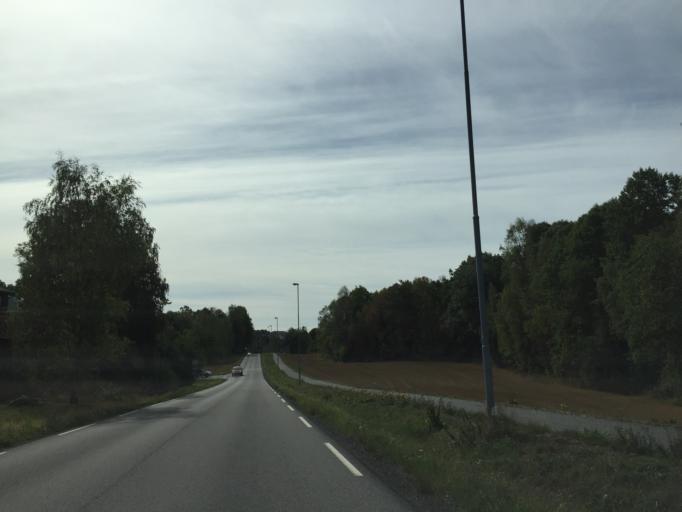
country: NO
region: Ostfold
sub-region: Moss
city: Moss
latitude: 59.4992
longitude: 10.6866
